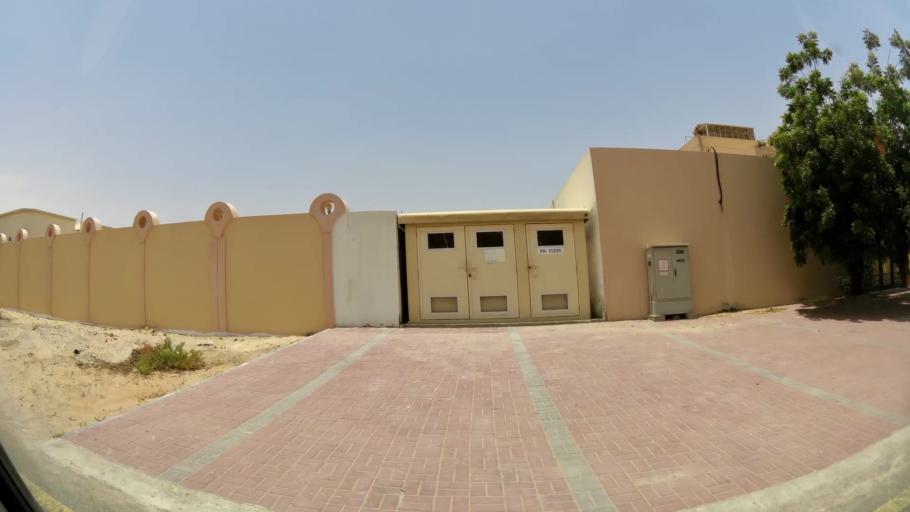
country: AE
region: Ash Shariqah
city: Sharjah
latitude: 25.2329
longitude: 55.4524
